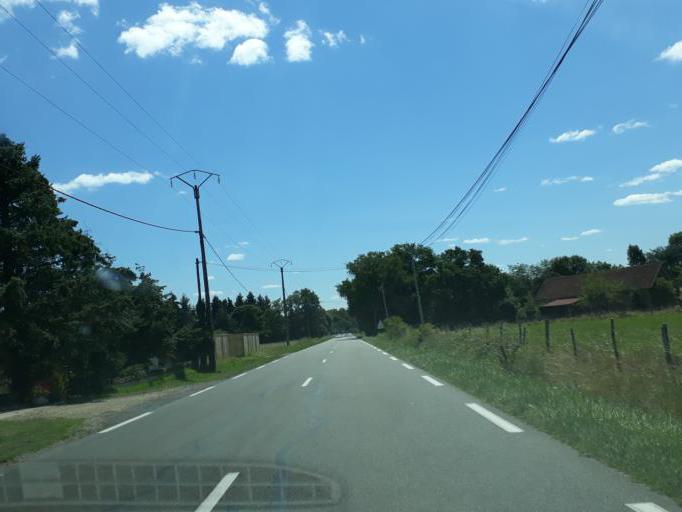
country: FR
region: Centre
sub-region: Departement du Loiret
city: Bray-en-Val
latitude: 47.8010
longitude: 2.3813
